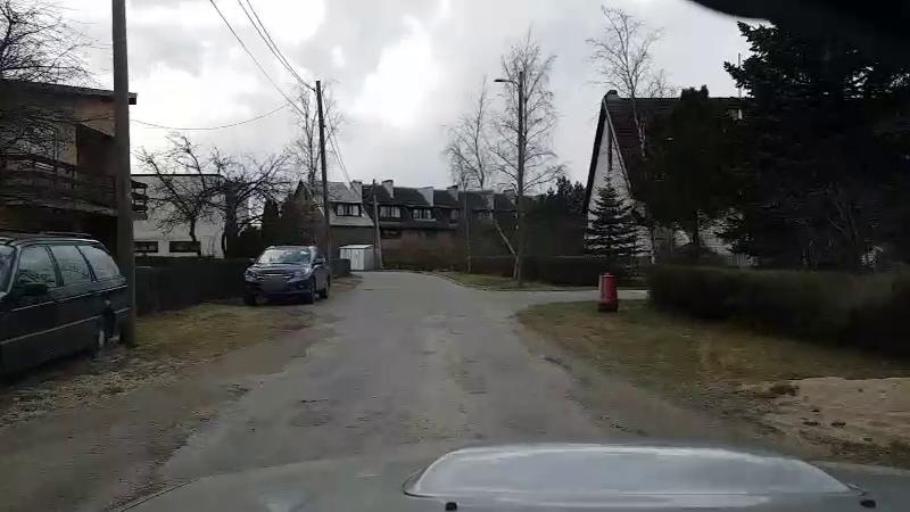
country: EE
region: Jaervamaa
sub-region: Paide linn
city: Paide
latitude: 58.8872
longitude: 25.5476
